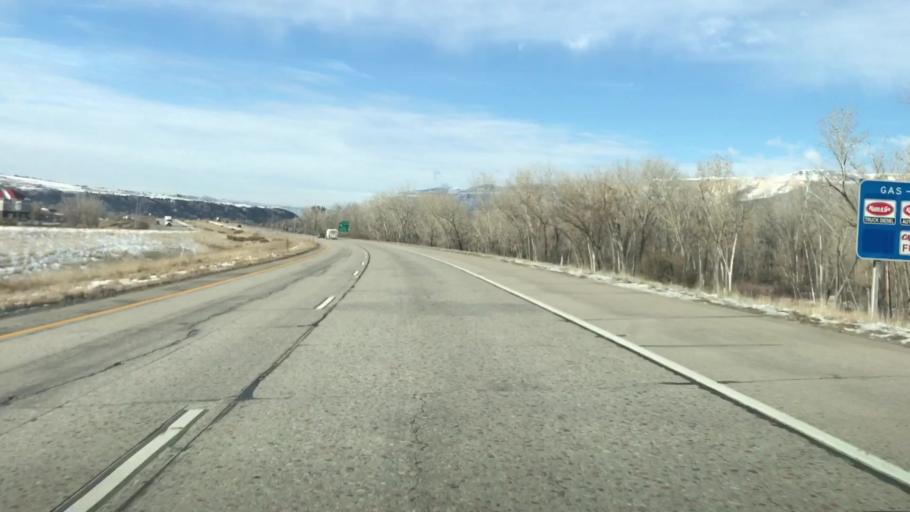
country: US
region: Colorado
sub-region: Garfield County
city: Rifle
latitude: 39.5264
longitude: -107.7685
